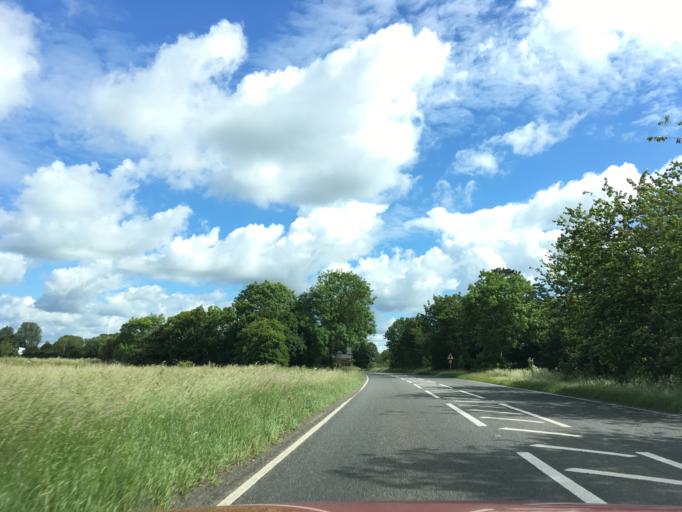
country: GB
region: England
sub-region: Gloucestershire
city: Lechlade
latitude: 51.7319
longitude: -1.6658
